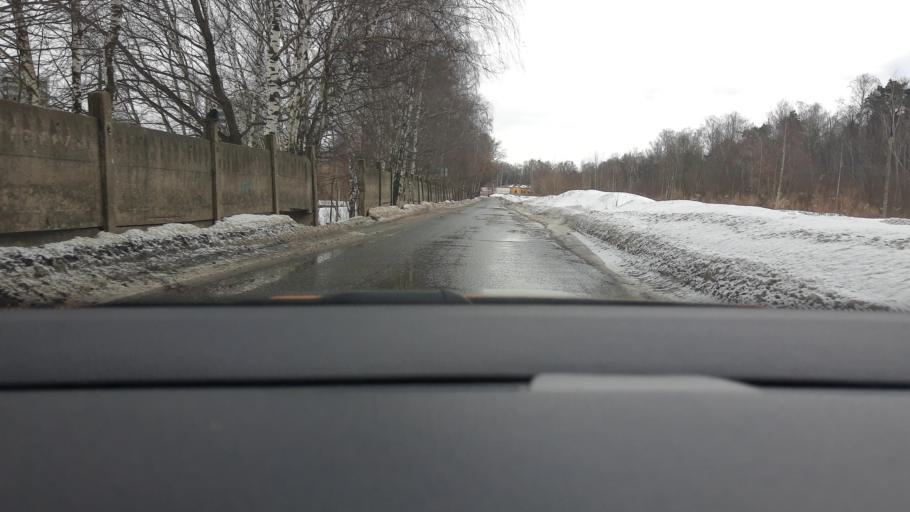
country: RU
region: Moscow
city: Babushkin
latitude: 55.8504
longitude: 37.7013
